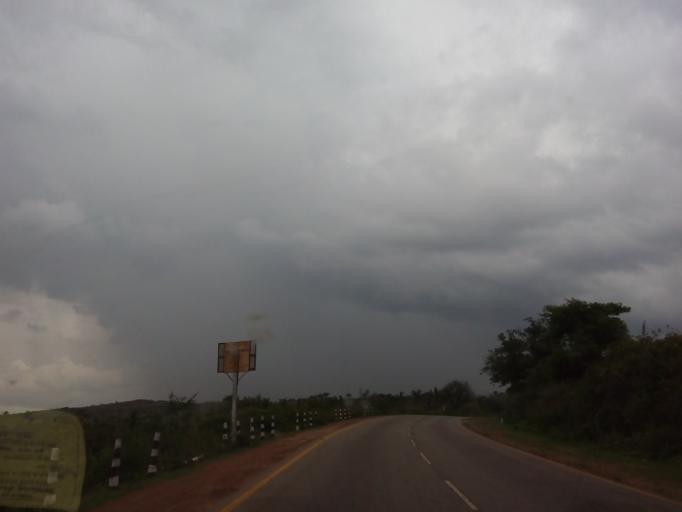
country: IN
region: Karnataka
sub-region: Hassan
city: Hassan
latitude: 13.0864
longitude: 76.0393
